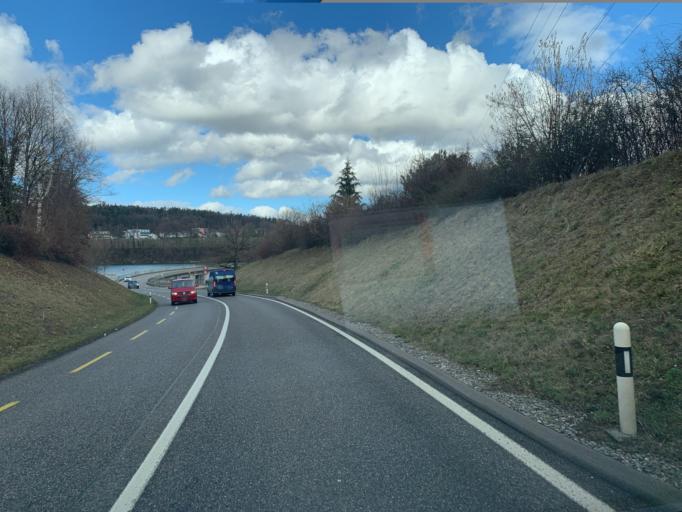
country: CH
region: Fribourg
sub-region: Sense District
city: Dudingen
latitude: 46.8793
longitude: 7.1929
